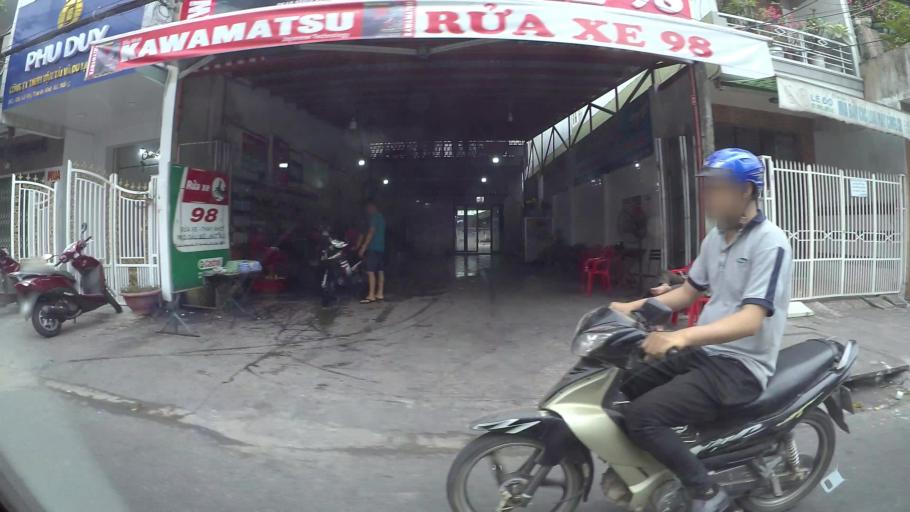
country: VN
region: Da Nang
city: Thanh Khe
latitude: 16.0682
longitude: 108.2015
